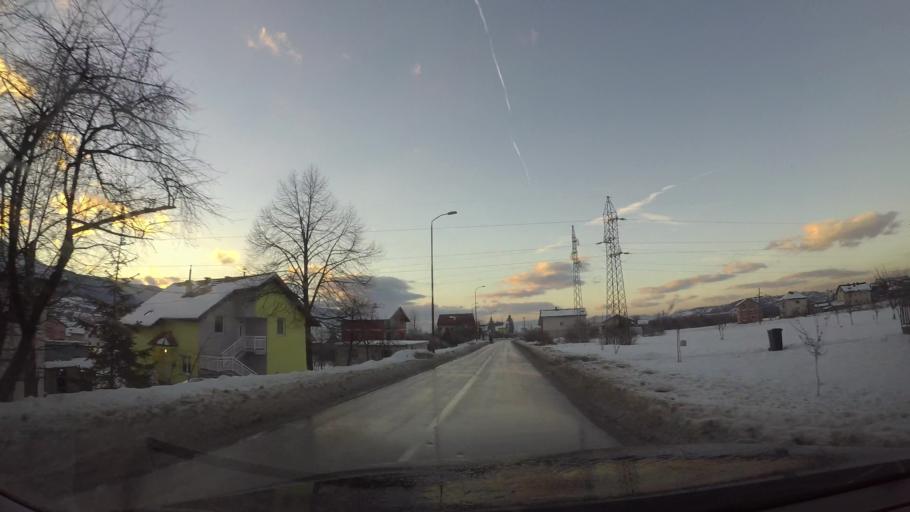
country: BA
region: Federation of Bosnia and Herzegovina
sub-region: Kanton Sarajevo
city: Sarajevo
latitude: 43.8103
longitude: 18.3732
